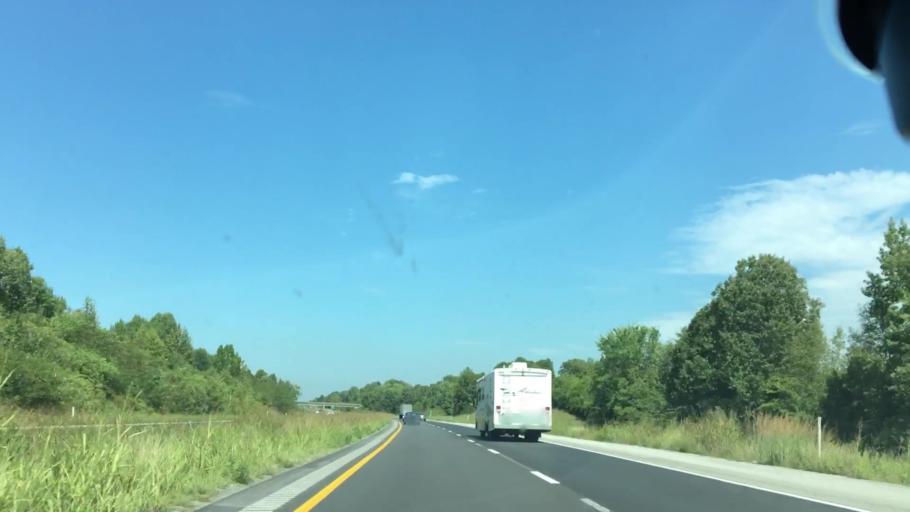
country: US
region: Kentucky
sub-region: Hopkins County
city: Madisonville
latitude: 37.3889
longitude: -87.4776
